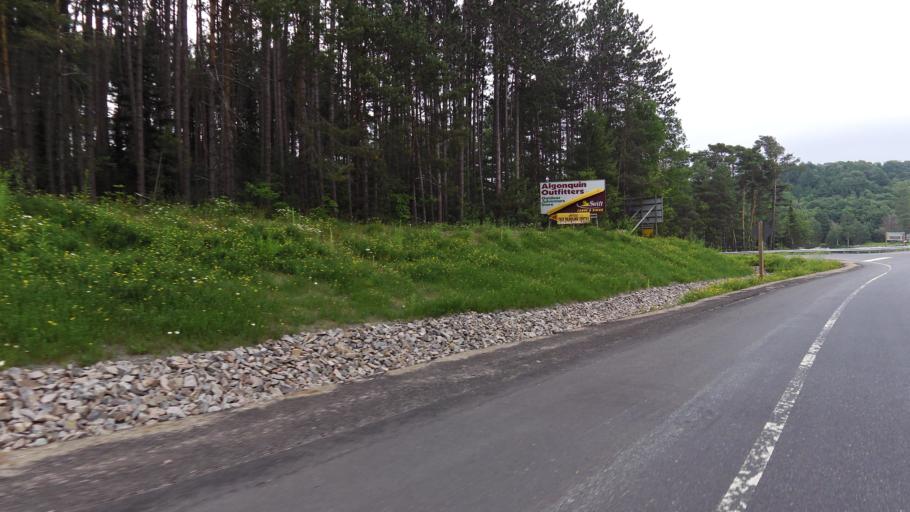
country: CA
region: Ontario
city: Huntsville
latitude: 45.3795
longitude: -78.9251
